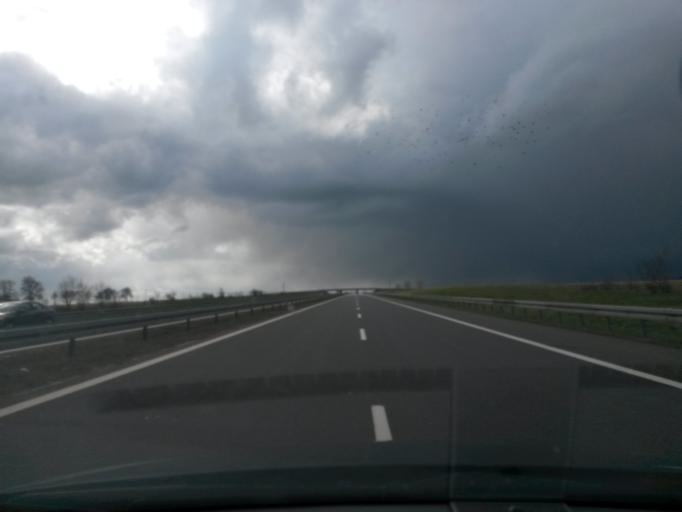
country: PL
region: Greater Poland Voivodeship
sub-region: Powiat sredzki
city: Dominowo
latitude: 52.3099
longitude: 17.3501
